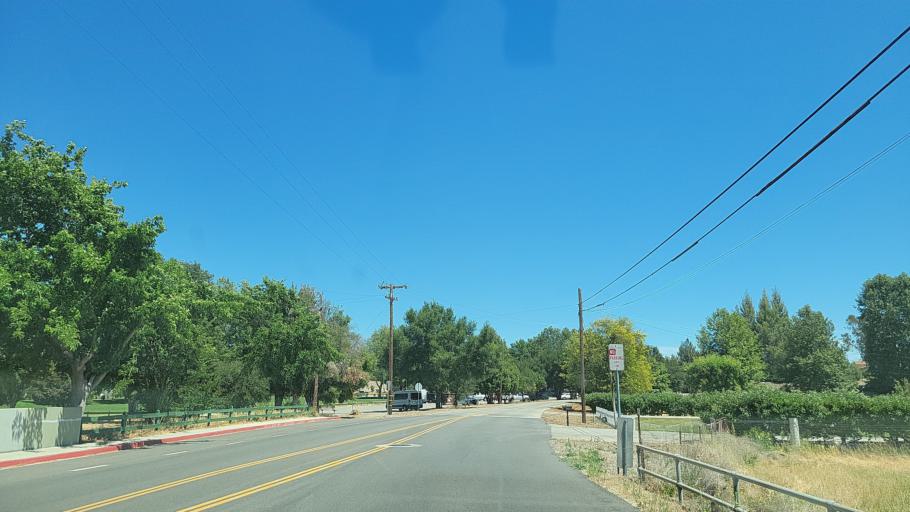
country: US
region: California
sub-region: San Luis Obispo County
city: Atascadero
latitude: 35.4540
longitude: -120.6365
